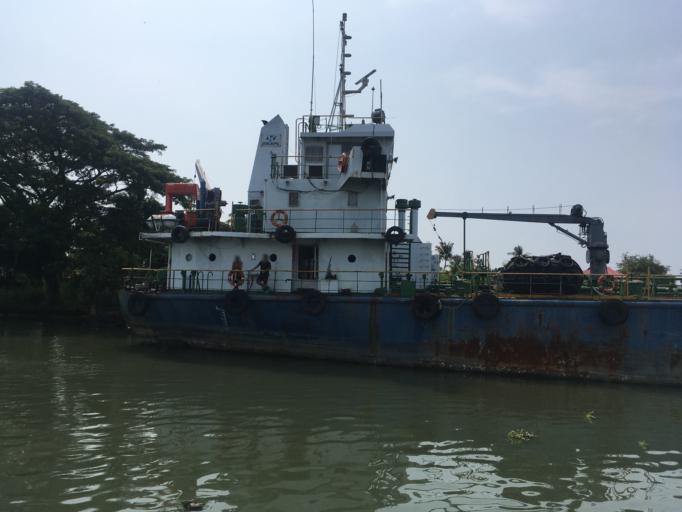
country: IN
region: Kerala
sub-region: Ernakulam
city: Cochin
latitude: 9.9767
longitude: 76.2438
